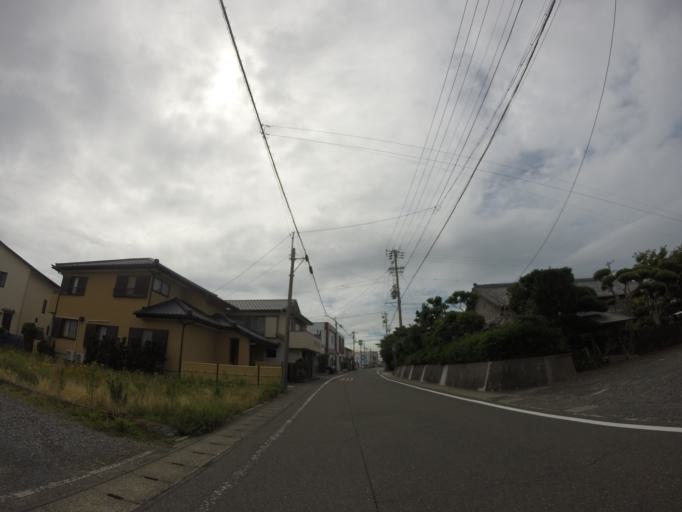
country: JP
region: Shizuoka
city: Oyama
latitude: 34.6034
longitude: 138.2168
